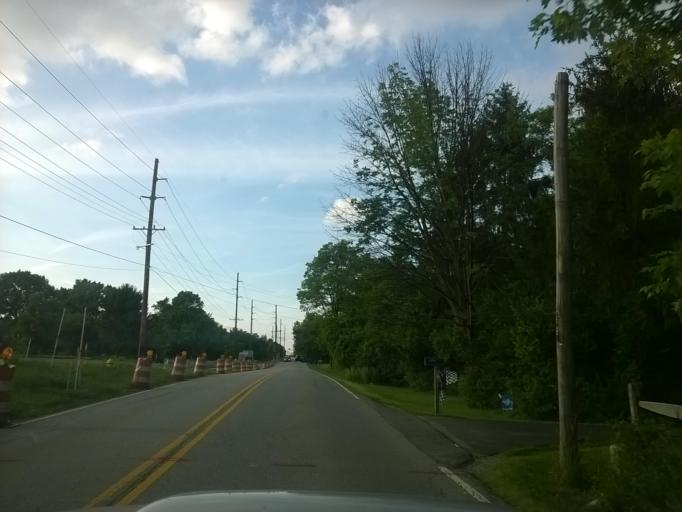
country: US
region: Indiana
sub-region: Hamilton County
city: Carmel
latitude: 39.9959
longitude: -86.0896
